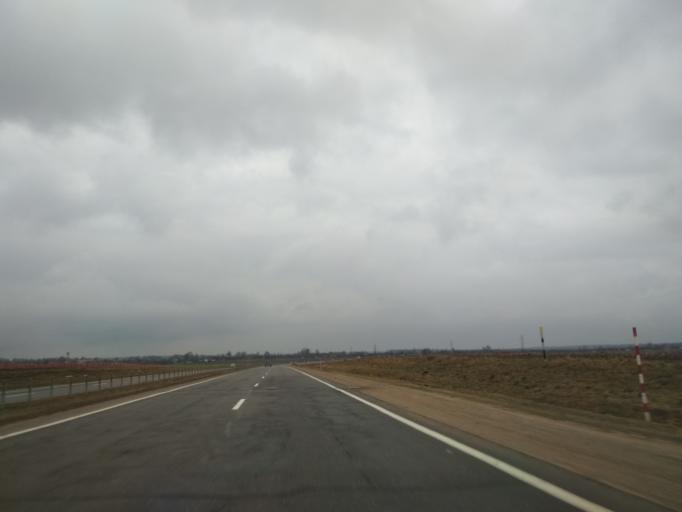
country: BY
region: Minsk
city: Dukora
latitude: 53.6797
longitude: 27.9238
